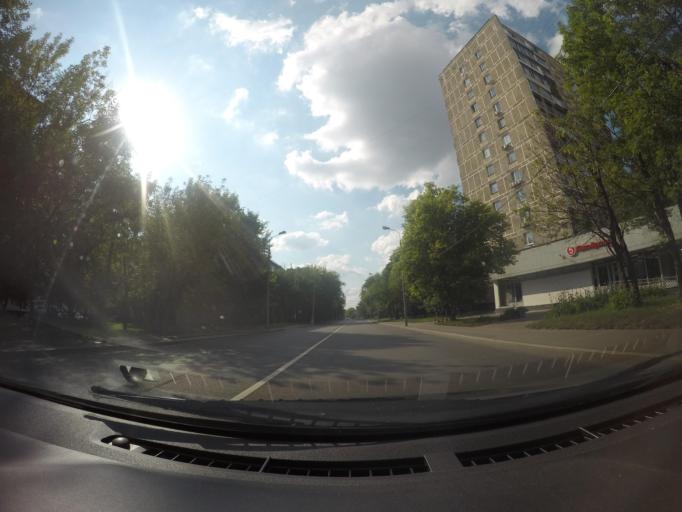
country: RU
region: Moscow
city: Sviblovo
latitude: 55.8363
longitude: 37.6413
